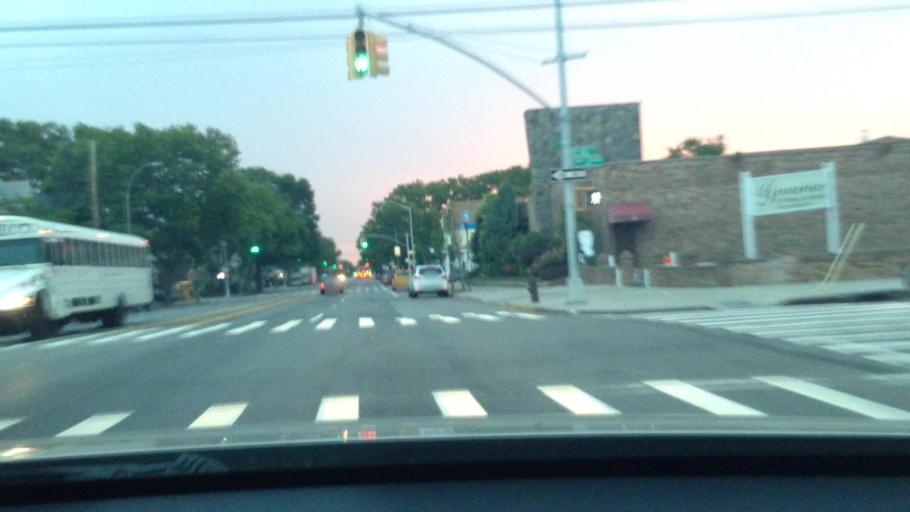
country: US
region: New York
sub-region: Kings County
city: East New York
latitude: 40.6410
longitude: -73.9047
